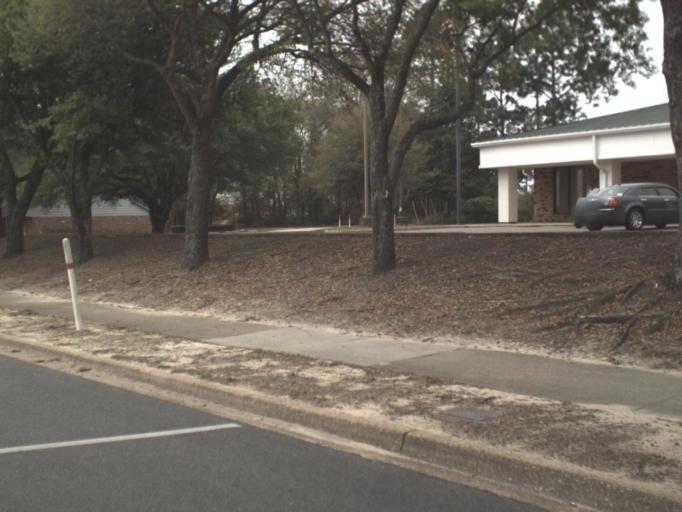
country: US
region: Florida
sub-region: Okaloosa County
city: Crestview
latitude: 30.7448
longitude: -86.5640
